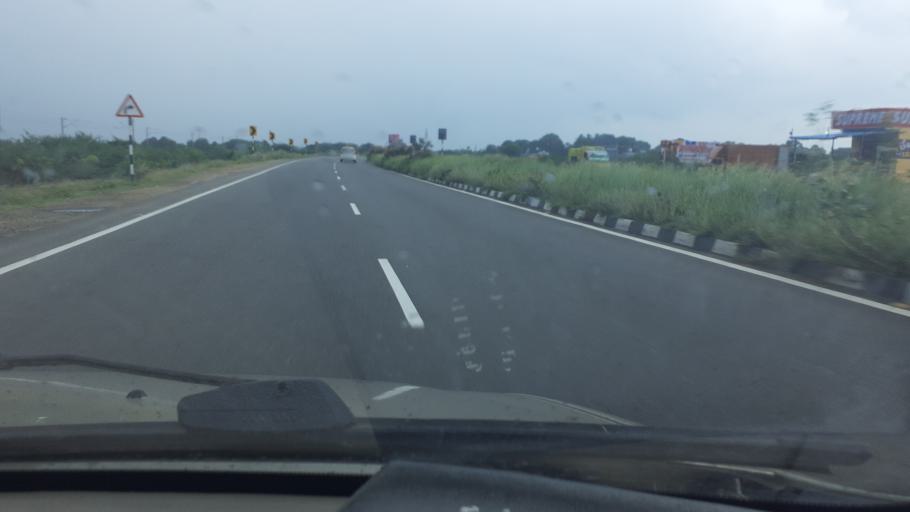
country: IN
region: Tamil Nadu
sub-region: Virudhunagar
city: Virudunagar
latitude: 9.6553
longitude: 77.9666
